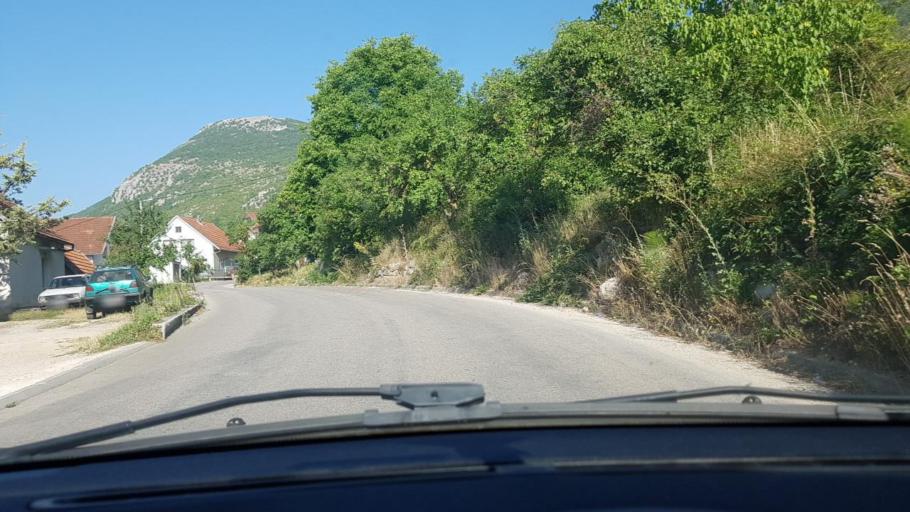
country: BA
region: Federation of Bosnia and Herzegovina
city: Rumboci
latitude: 43.8297
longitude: 17.5039
